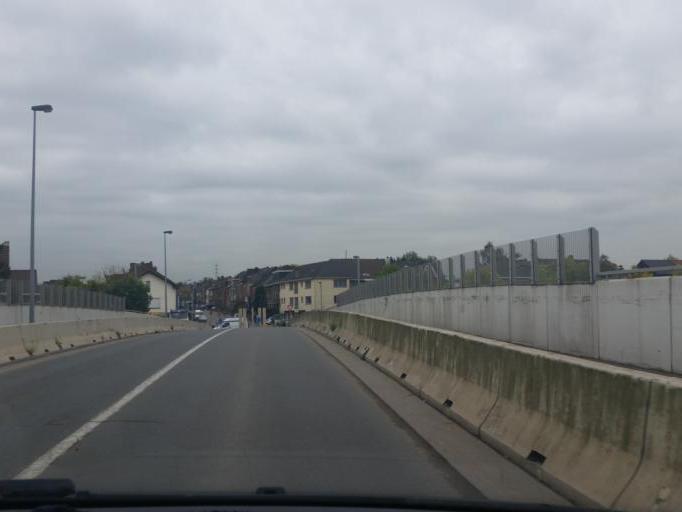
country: BE
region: Flanders
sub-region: Provincie Vlaams-Brabant
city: Halle
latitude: 50.7376
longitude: 4.2442
